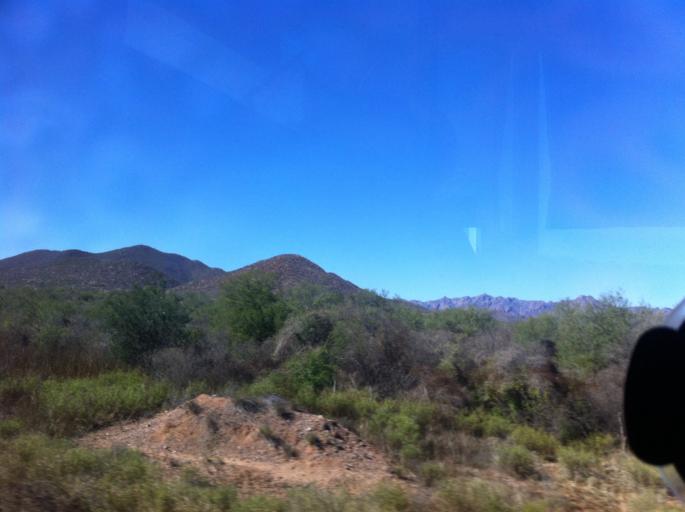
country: MX
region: Sonora
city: Heroica Guaymas
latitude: 28.0182
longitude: -110.9316
